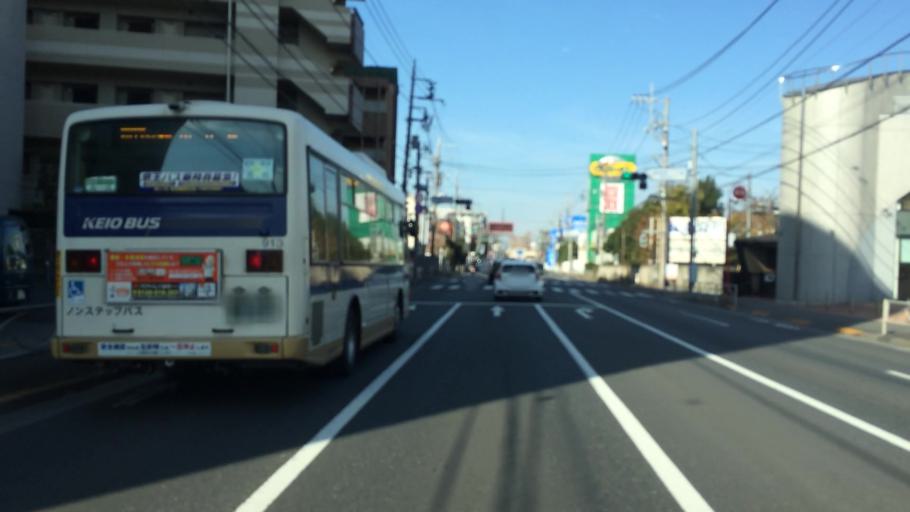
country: JP
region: Tokyo
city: Kokubunji
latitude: 35.6742
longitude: 139.4570
